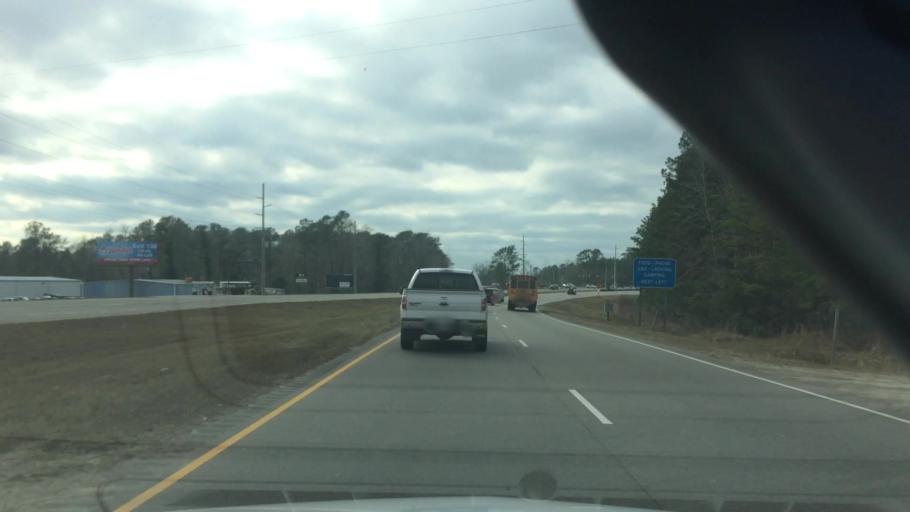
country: US
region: North Carolina
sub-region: Brunswick County
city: Shallotte
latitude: 33.9872
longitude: -78.3596
